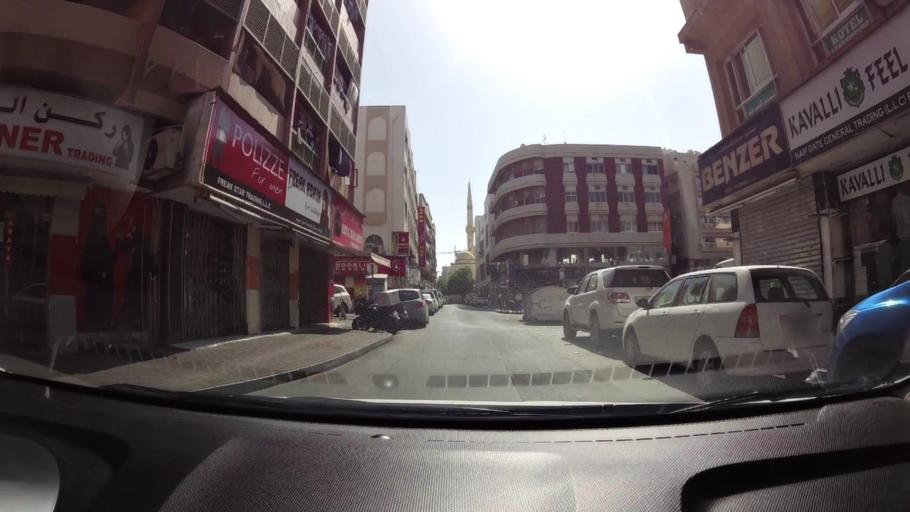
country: AE
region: Ash Shariqah
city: Sharjah
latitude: 25.2728
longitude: 55.3038
